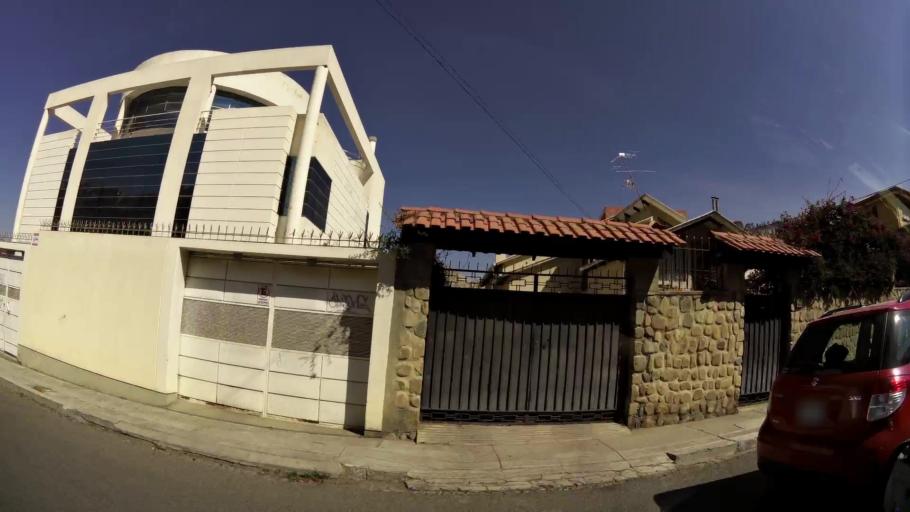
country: BO
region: La Paz
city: La Paz
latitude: -16.5204
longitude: -68.0856
